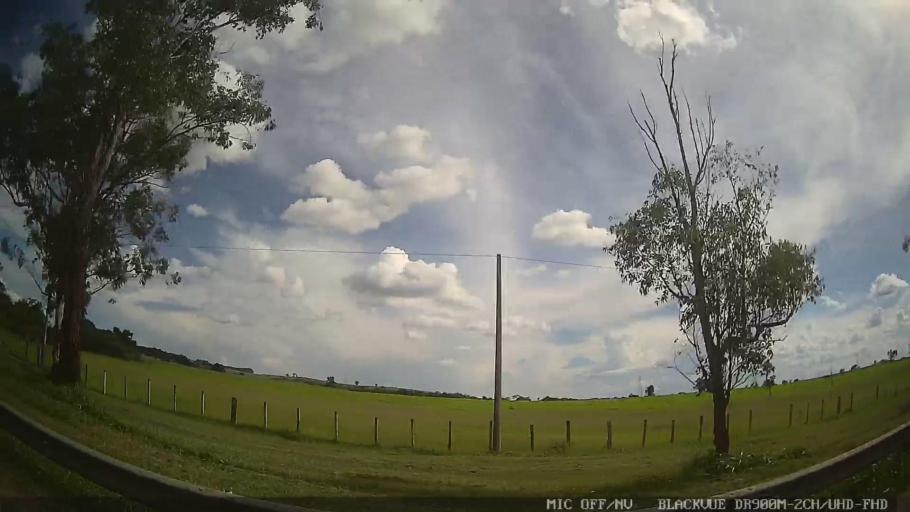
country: BR
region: Sao Paulo
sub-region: Conchas
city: Conchas
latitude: -23.0451
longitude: -47.9356
